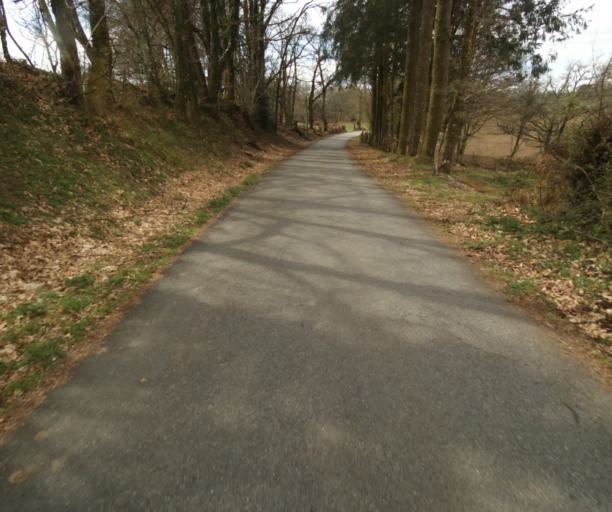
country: FR
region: Limousin
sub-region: Departement de la Correze
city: Correze
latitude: 45.3922
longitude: 1.8992
